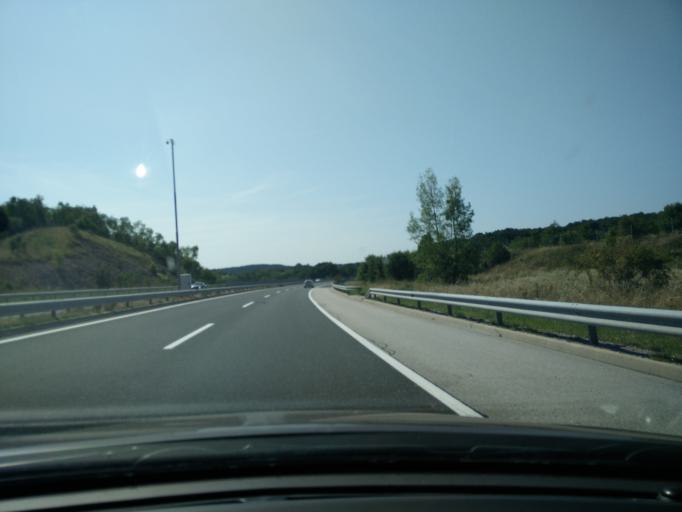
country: SI
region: Hrpelje-Kozina
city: Kozina
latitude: 45.5888
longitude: 13.9298
